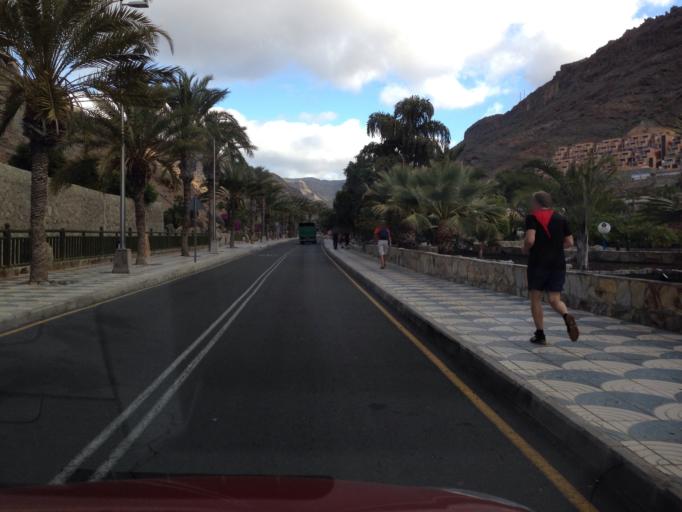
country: ES
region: Canary Islands
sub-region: Provincia de Las Palmas
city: Puerto Rico
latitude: 27.8172
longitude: -15.7524
